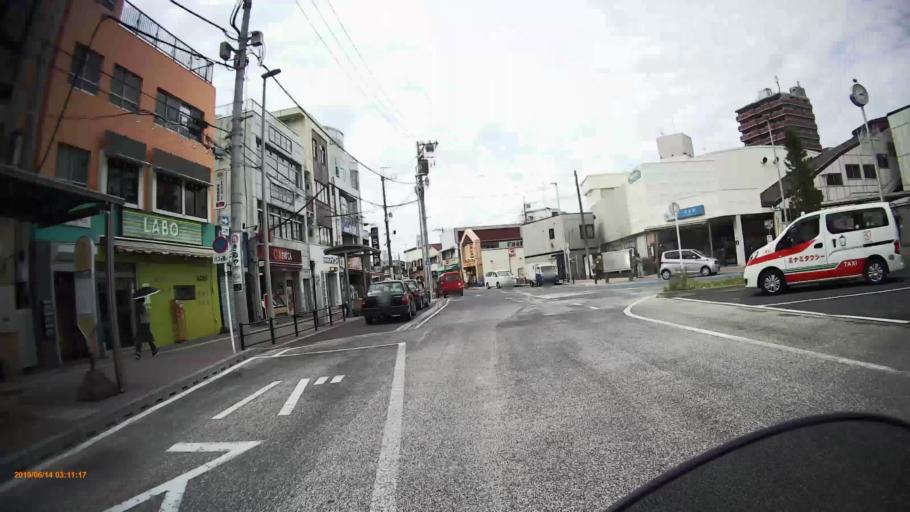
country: JP
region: Kanagawa
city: Fujisawa
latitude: 35.4124
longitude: 139.4648
